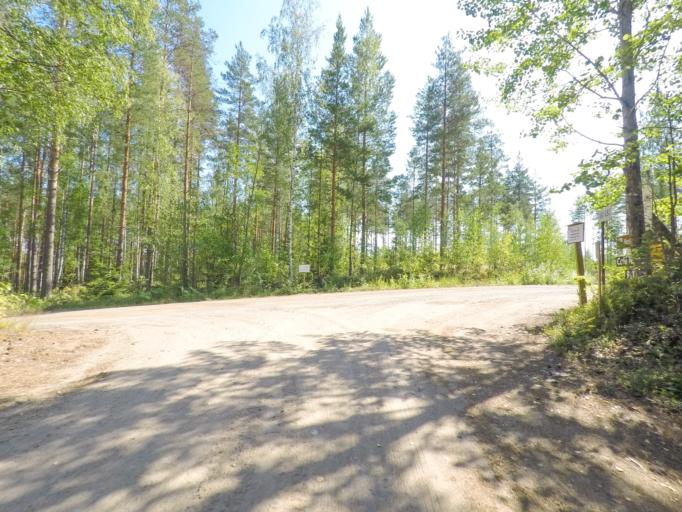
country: FI
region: Southern Savonia
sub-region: Mikkeli
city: Puumala
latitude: 61.4266
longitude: 28.0134
